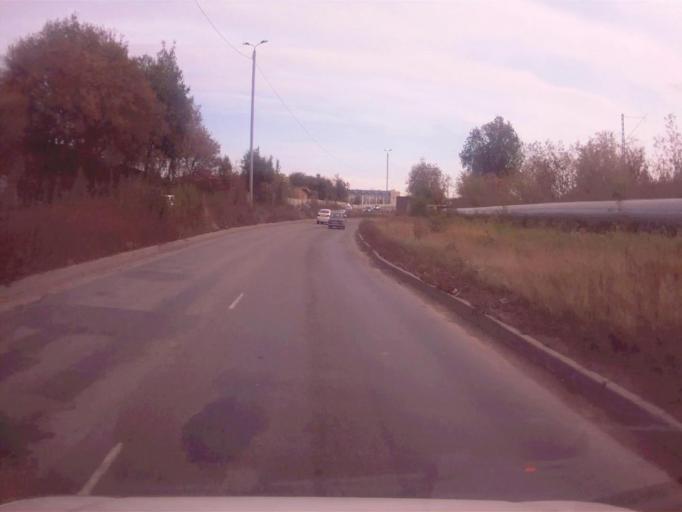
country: RU
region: Chelyabinsk
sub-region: Gorod Chelyabinsk
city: Chelyabinsk
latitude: 55.1588
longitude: 61.4362
